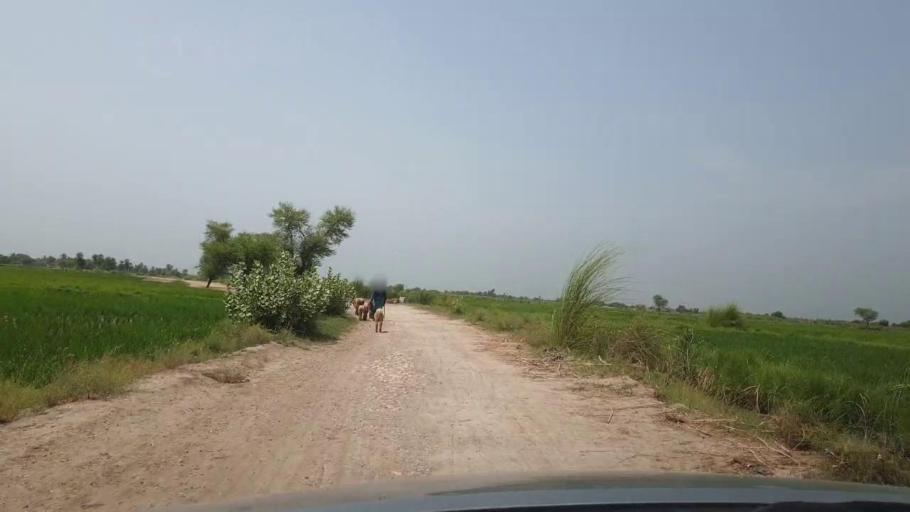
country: PK
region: Sindh
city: Madeji
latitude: 27.7945
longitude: 68.4354
